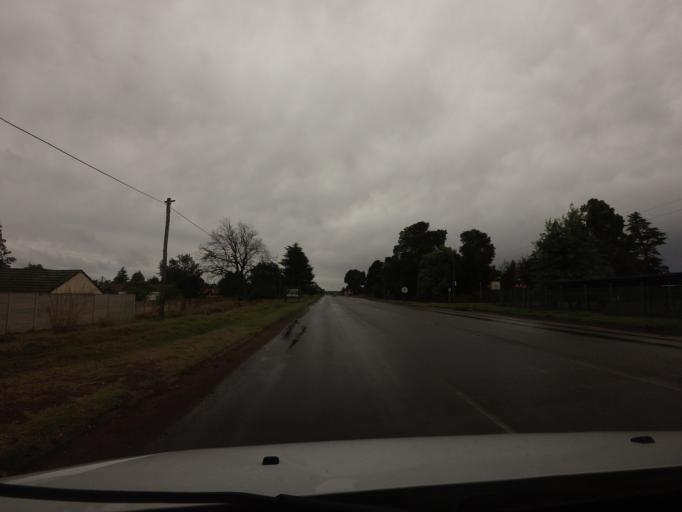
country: ZA
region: Mpumalanga
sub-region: Nkangala District Municipality
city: Belfast
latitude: -25.7016
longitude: 30.0453
